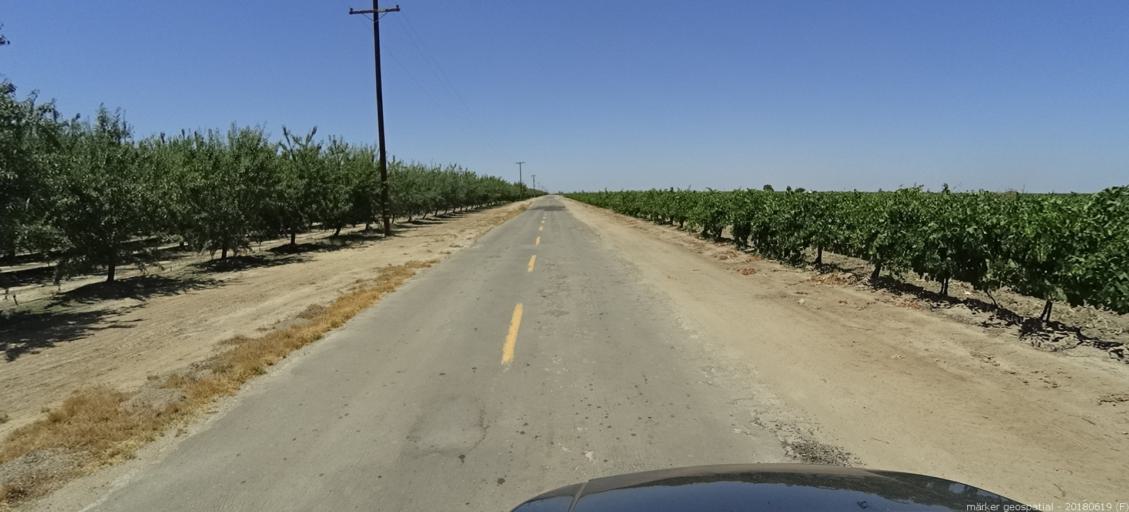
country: US
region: California
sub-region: Madera County
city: Parkwood
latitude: 36.8658
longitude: -120.1481
